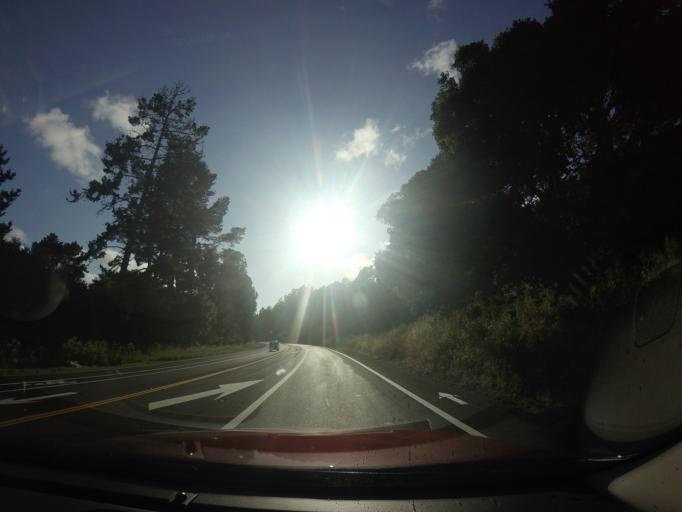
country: US
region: California
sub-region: Monterey County
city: Carmel-by-the-Sea
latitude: 36.5402
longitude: -121.8669
